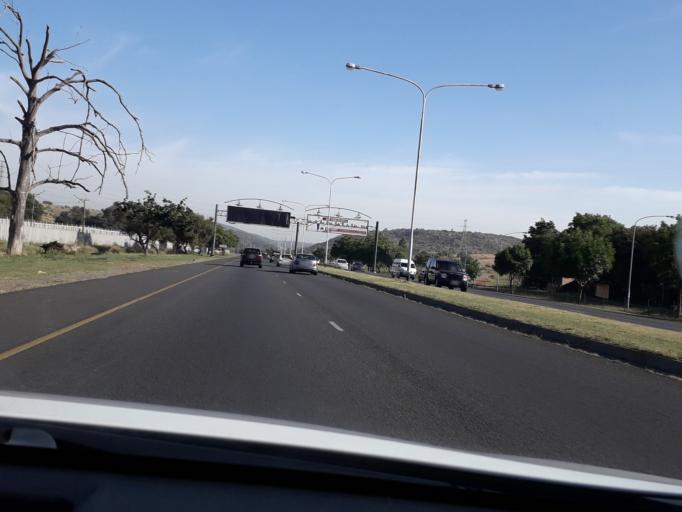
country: ZA
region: Gauteng
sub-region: City of Tshwane Metropolitan Municipality
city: Centurion
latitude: -25.8127
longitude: 28.2015
